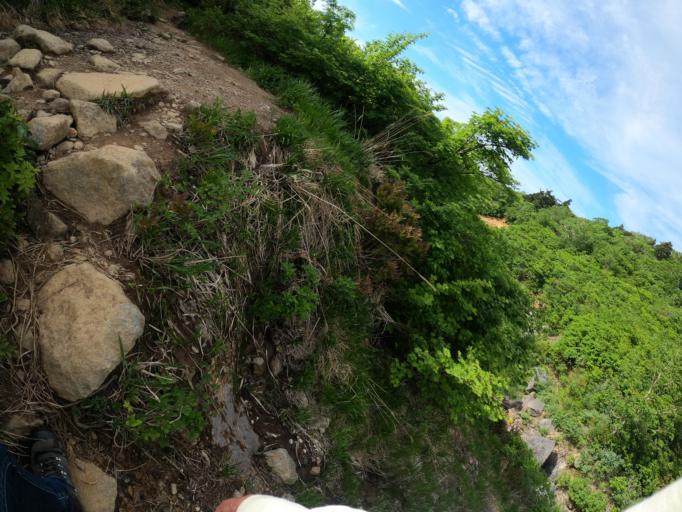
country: JP
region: Akita
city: Yuzawa
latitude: 38.9740
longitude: 140.7787
